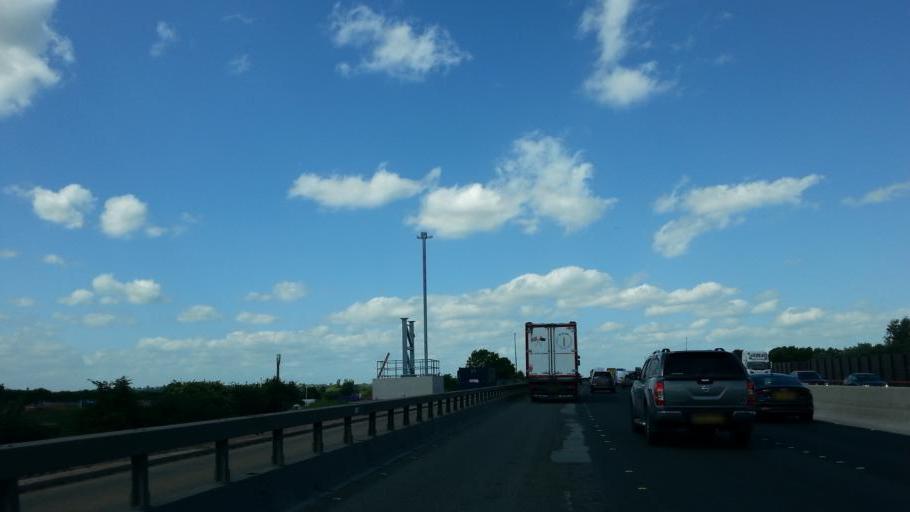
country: GB
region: England
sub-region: Derbyshire
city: Long Eaton
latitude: 52.8830
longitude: -1.3098
